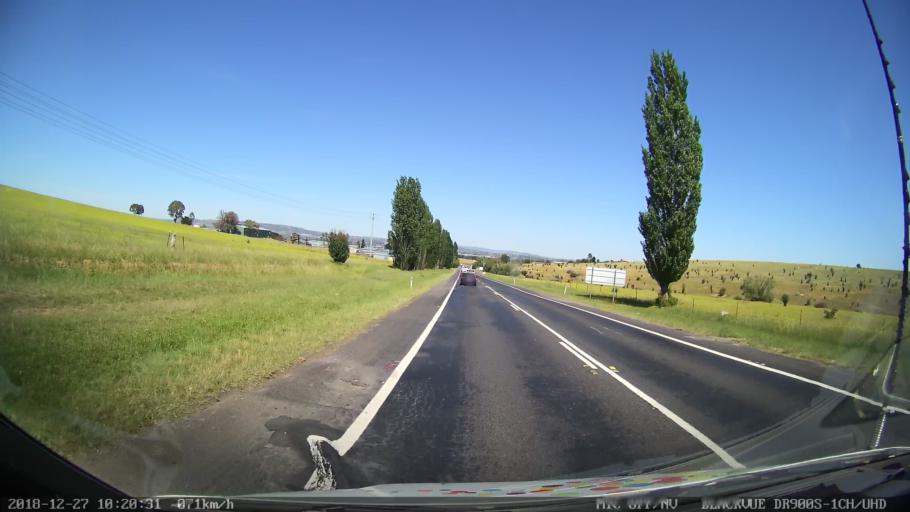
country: AU
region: New South Wales
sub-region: Bathurst Regional
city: Kelso
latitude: -33.4215
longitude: 149.6352
